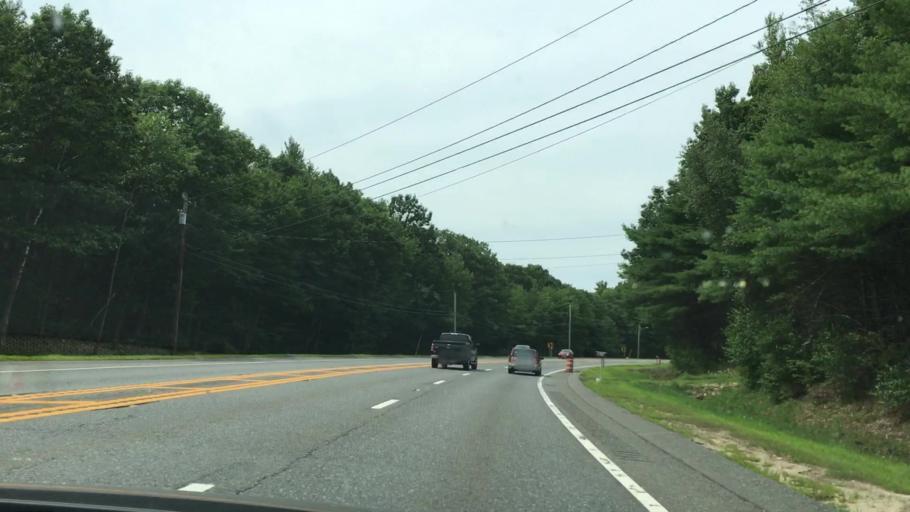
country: US
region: Massachusetts
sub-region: Worcester County
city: Gardner
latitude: 42.6172
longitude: -72.0071
